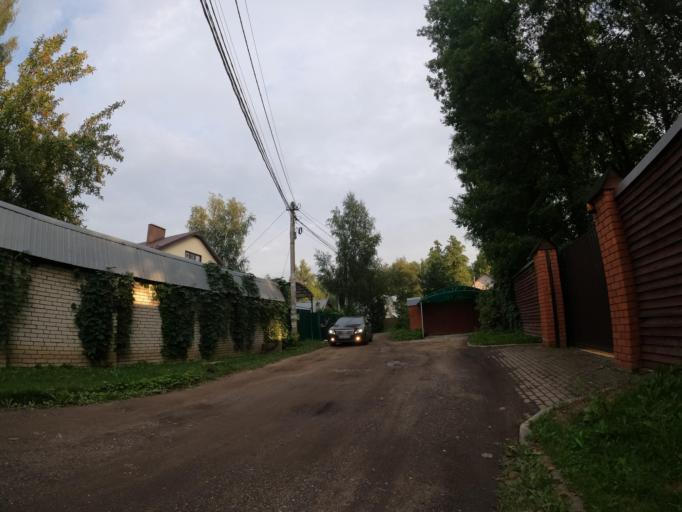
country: RU
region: Moskovskaya
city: Bykovo
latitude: 55.6380
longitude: 38.0873
